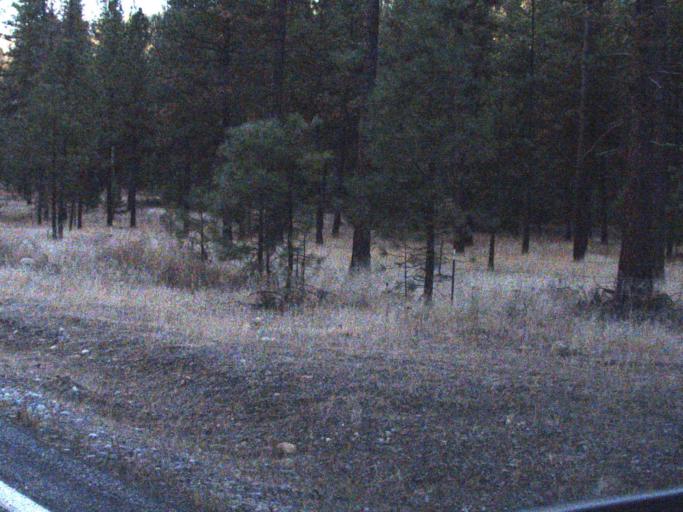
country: US
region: Washington
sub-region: Ferry County
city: Republic
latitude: 48.3223
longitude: -118.7429
